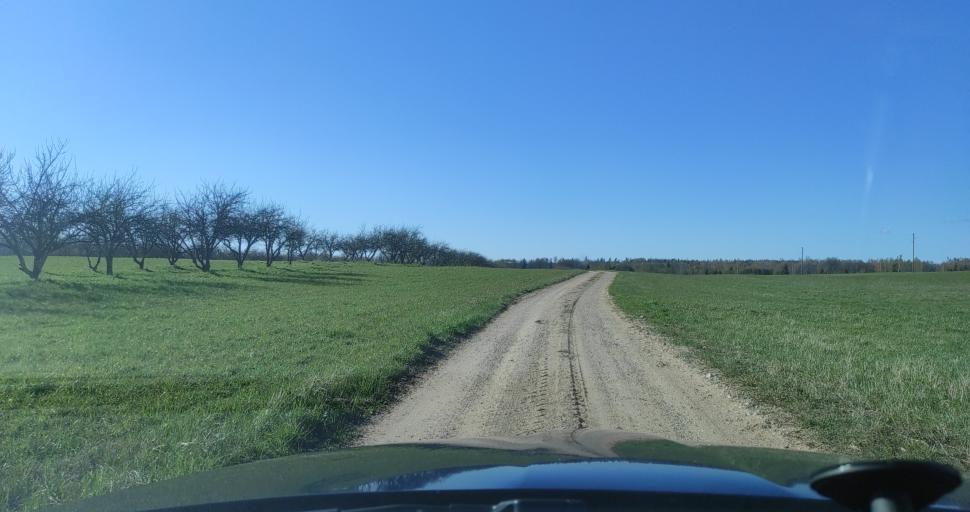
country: LV
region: Kuldigas Rajons
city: Kuldiga
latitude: 56.8698
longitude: 21.8412
